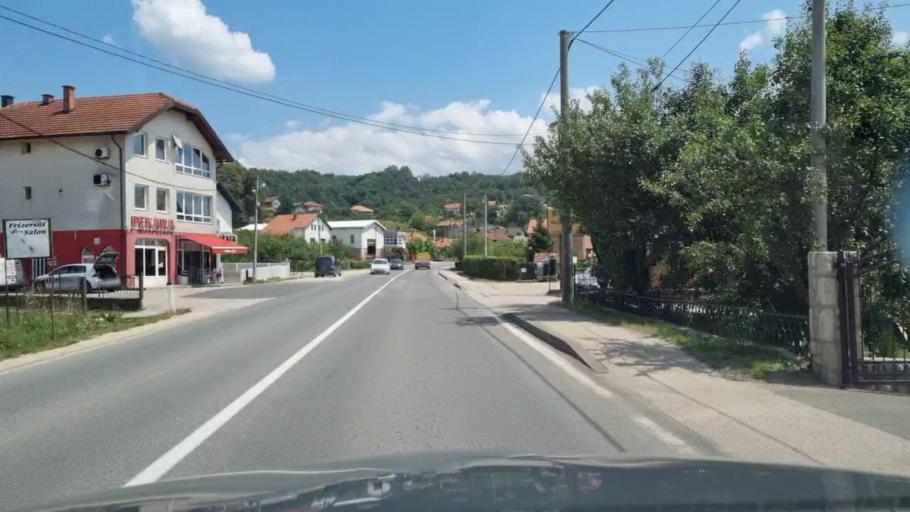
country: BA
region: Federation of Bosnia and Herzegovina
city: Orahovica Donja
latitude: 44.6431
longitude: 18.3786
